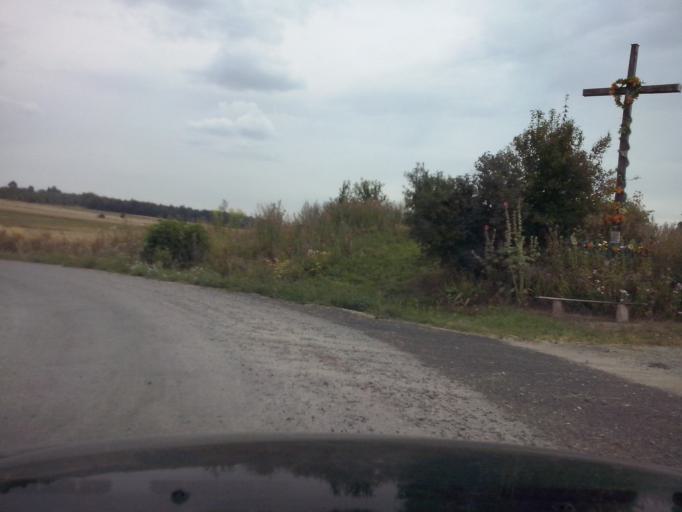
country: PL
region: Swietokrzyskie
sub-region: Powiat kielecki
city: Lagow
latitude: 50.7344
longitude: 21.0514
